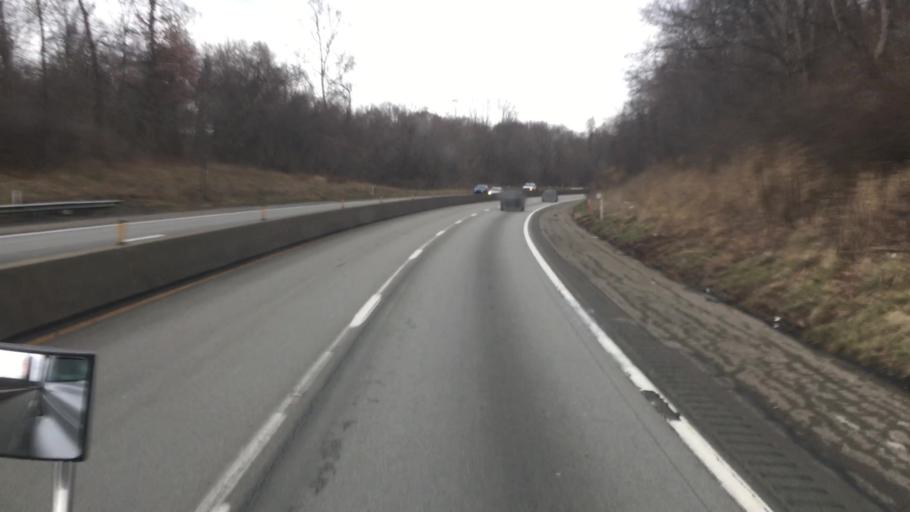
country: US
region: Pennsylvania
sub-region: Westmoreland County
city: West Newton
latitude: 40.1929
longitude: -79.6874
